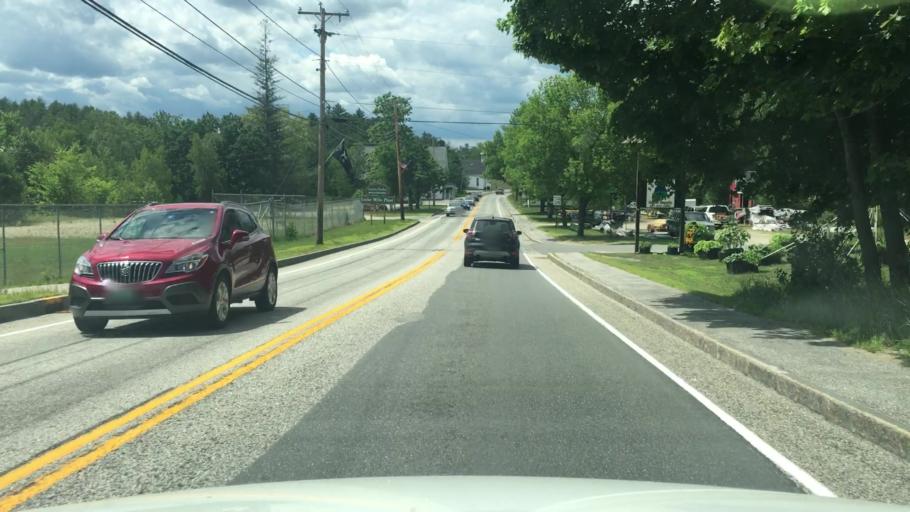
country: US
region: Maine
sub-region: Oxford County
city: Bethel
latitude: 44.4004
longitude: -70.7031
